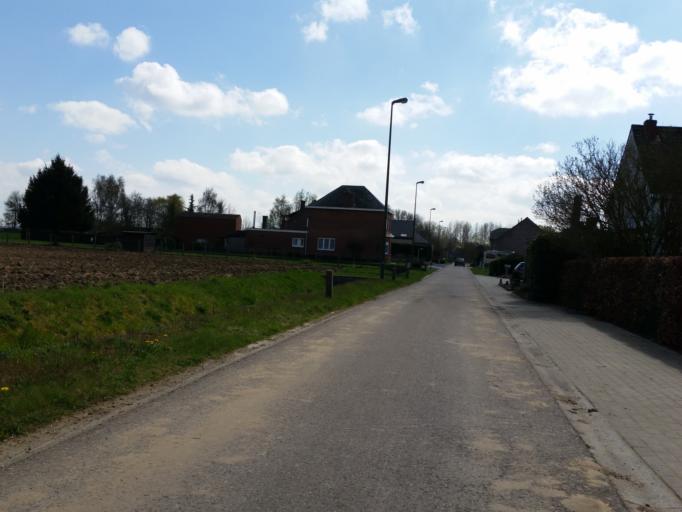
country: BE
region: Flanders
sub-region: Provincie Vlaams-Brabant
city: Boortmeerbeek
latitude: 50.9507
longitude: 4.5947
